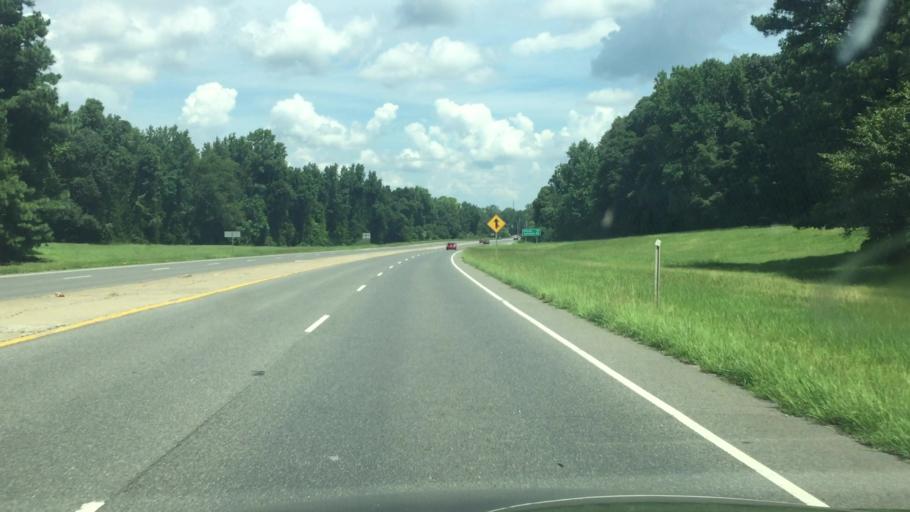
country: US
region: North Carolina
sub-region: Richmond County
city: Rockingham
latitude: 34.9326
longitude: -79.7805
